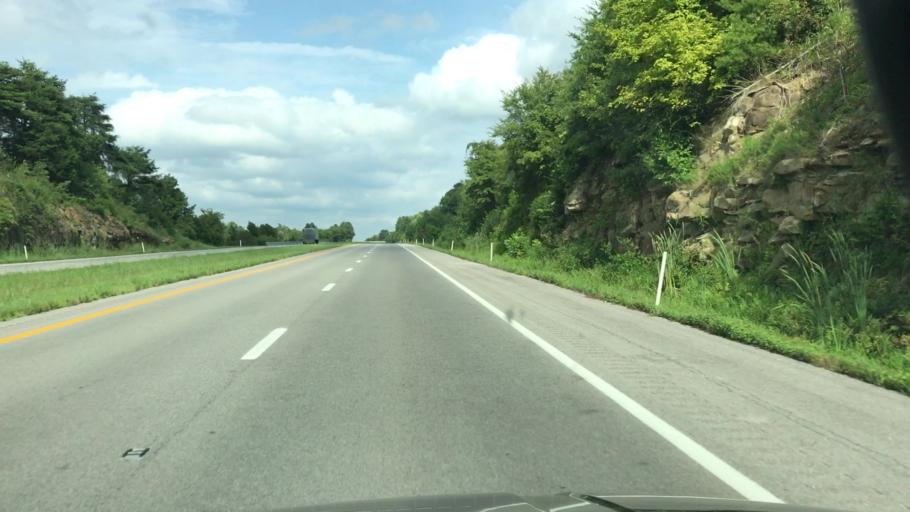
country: US
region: Kentucky
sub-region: Hopkins County
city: Dawson Springs
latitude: 37.1670
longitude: -87.7518
